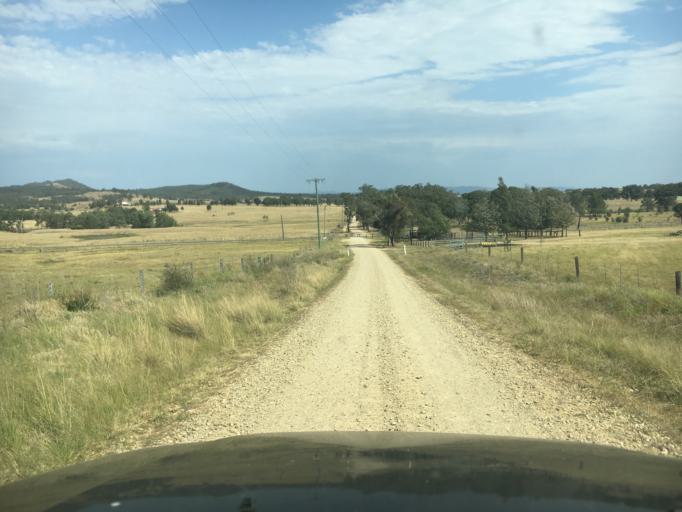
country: AU
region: New South Wales
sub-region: Cessnock
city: Branxton
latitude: -32.5060
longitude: 151.3159
